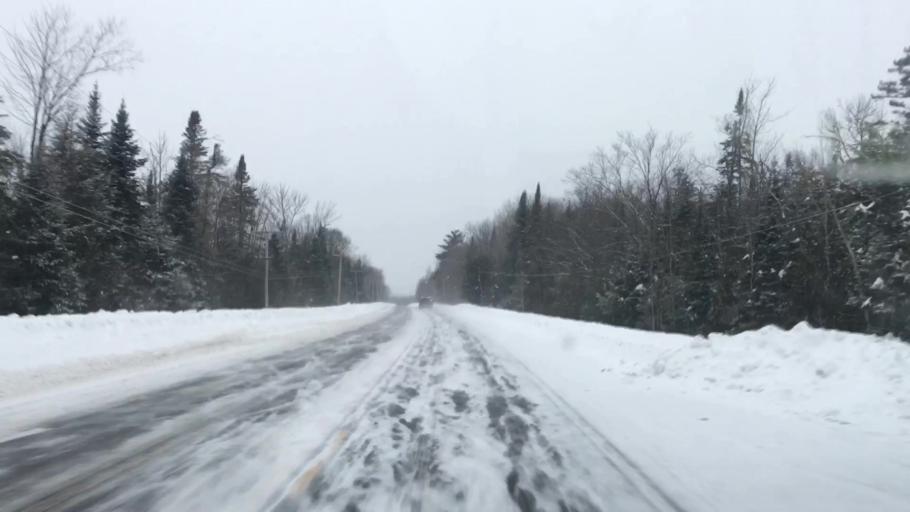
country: US
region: Maine
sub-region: Penobscot County
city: Medway
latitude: 45.5849
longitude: -68.4294
